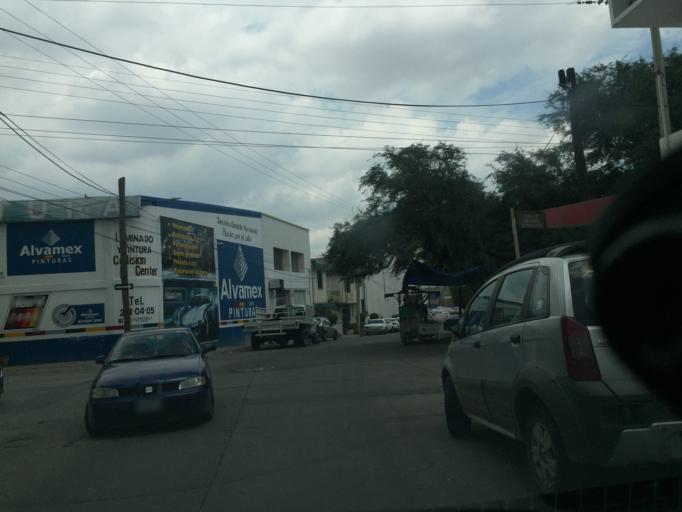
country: MX
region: Guanajuato
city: Leon
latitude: 21.1413
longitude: -101.6907
